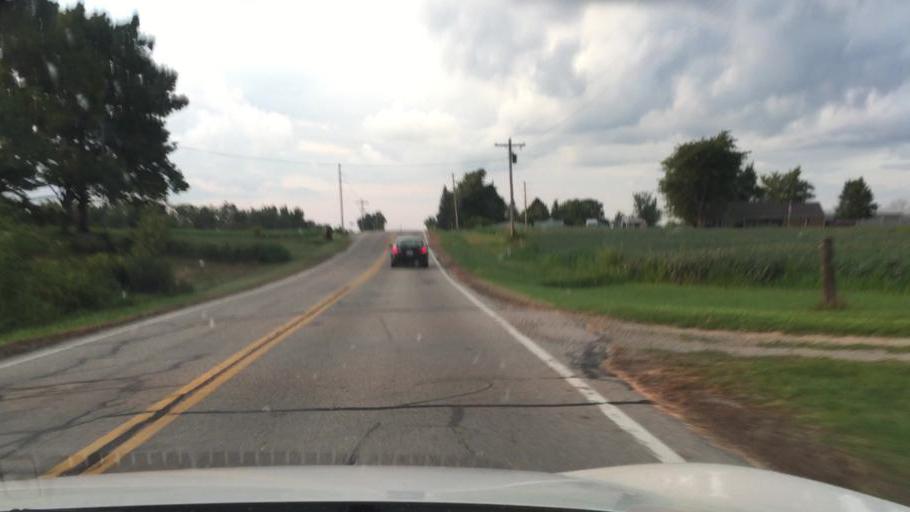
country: US
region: Ohio
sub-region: Champaign County
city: Mechanicsburg
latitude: 40.0469
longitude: -83.5678
